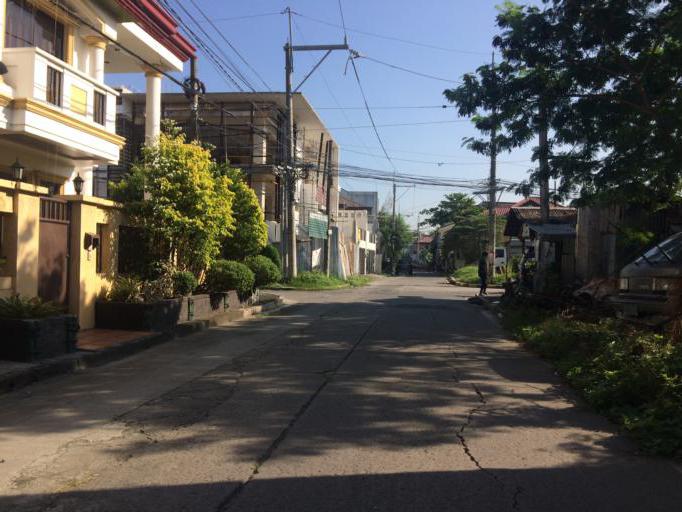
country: PH
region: Calabarzon
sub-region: Province of Rizal
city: Taytay
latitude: 14.5533
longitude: 121.1091
